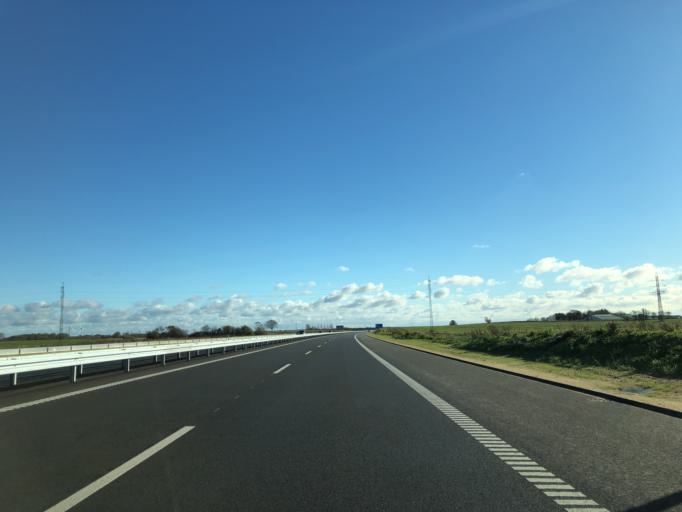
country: DK
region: Central Jutland
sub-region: Holstebro Kommune
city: Holstebro
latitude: 56.3768
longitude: 8.6976
